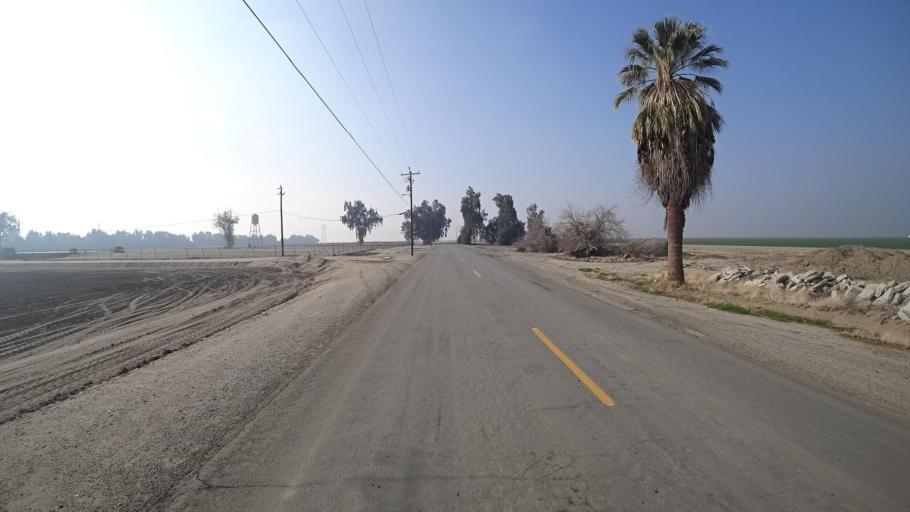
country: US
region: California
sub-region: Kern County
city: Greenfield
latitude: 35.1507
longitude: -119.0082
